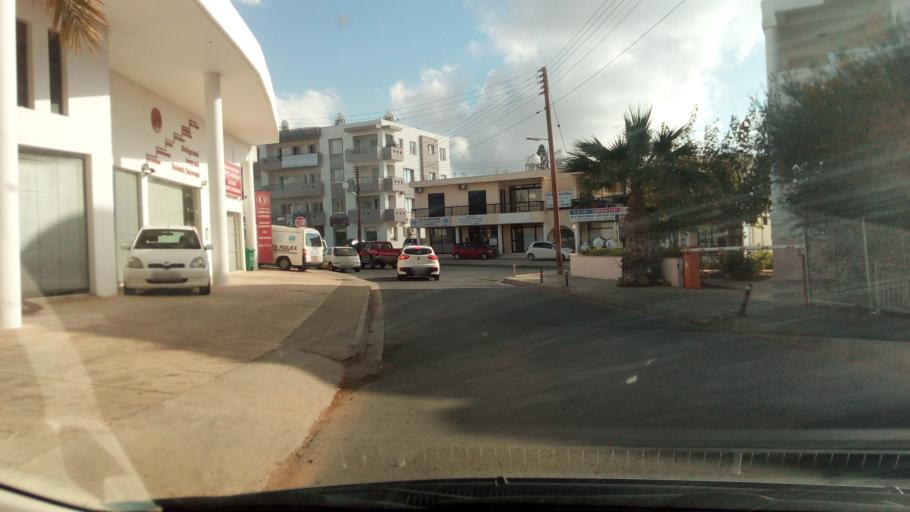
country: CY
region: Pafos
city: Paphos
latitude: 34.7835
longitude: 32.4300
